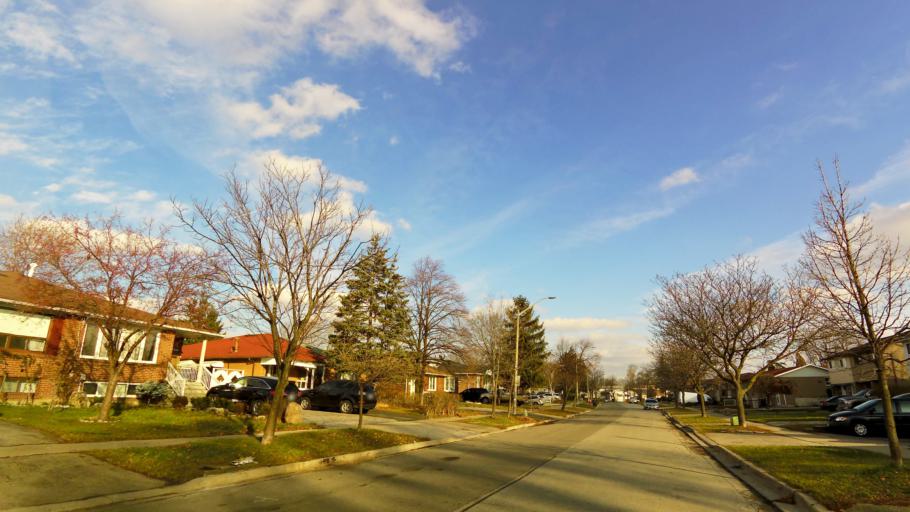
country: CA
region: Ontario
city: Mississauga
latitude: 43.5645
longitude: -79.6570
